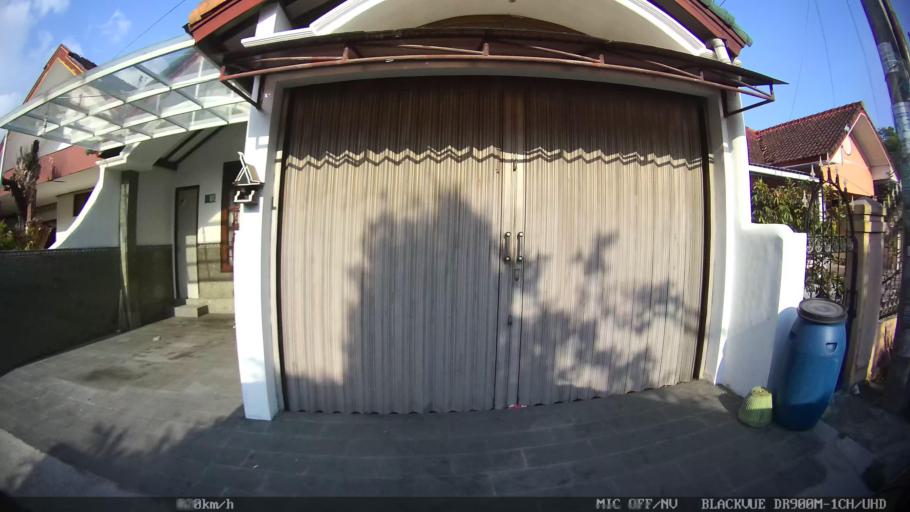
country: ID
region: Daerah Istimewa Yogyakarta
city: Gamping Lor
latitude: -7.7956
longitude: 110.3329
